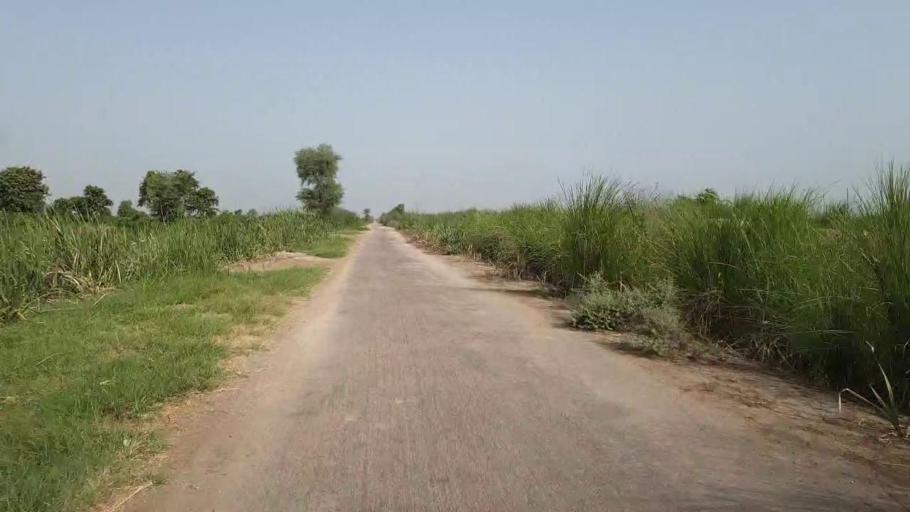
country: PK
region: Sindh
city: Daur
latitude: 26.3487
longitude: 68.1752
